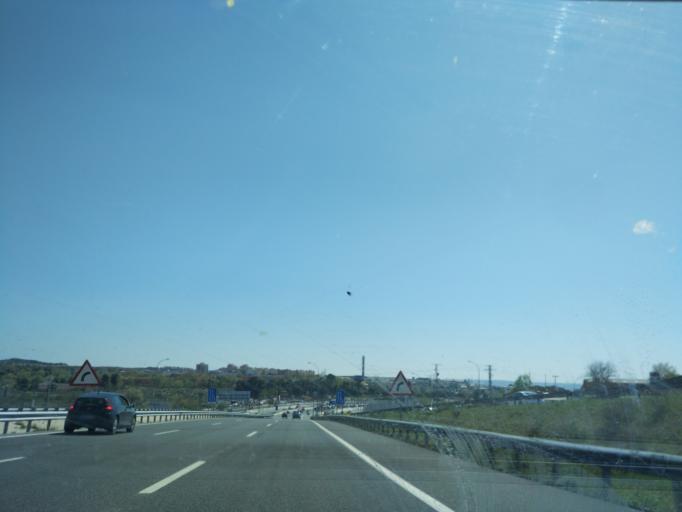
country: ES
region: Madrid
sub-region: Provincia de Madrid
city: Villa de Vallecas
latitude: 40.3587
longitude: -3.5601
